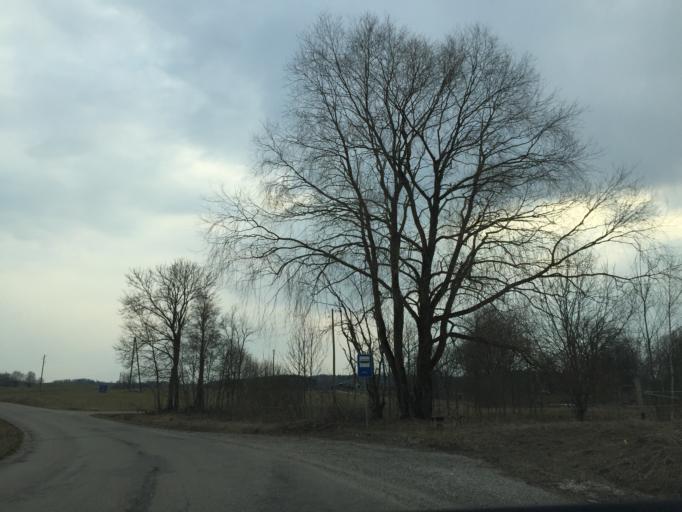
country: LV
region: Priekuli
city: Priekuli
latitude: 57.2452
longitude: 25.3724
